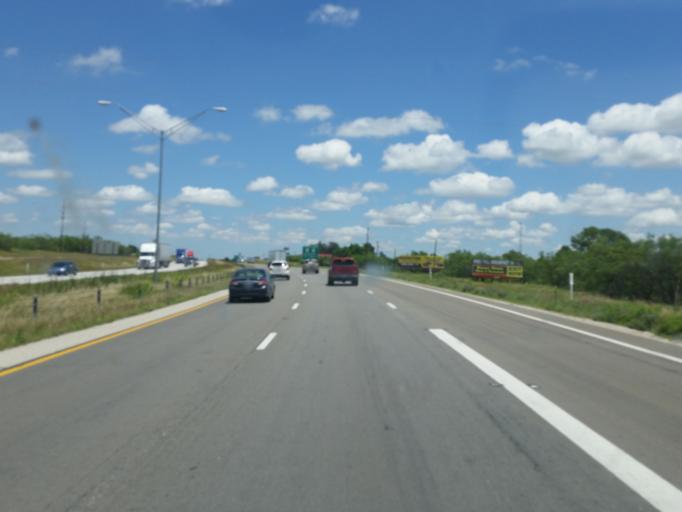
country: US
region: Texas
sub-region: Nolan County
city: Sweetwater
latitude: 32.4475
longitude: -100.4122
